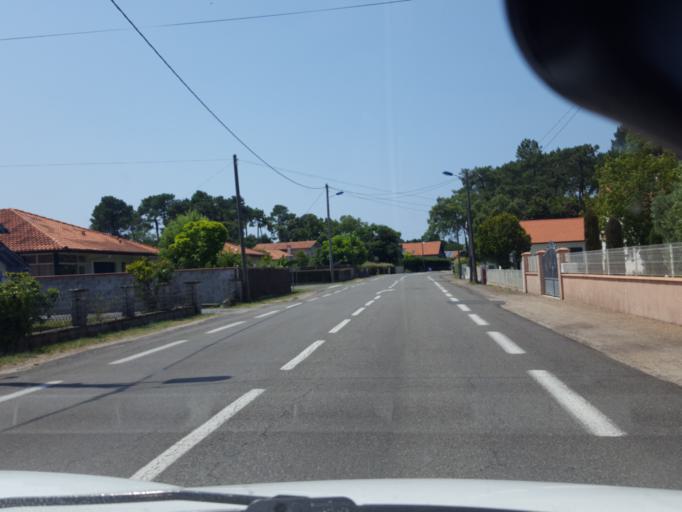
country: FR
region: Aquitaine
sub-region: Departement des Landes
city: Ondres
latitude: 43.5703
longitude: -1.4654
